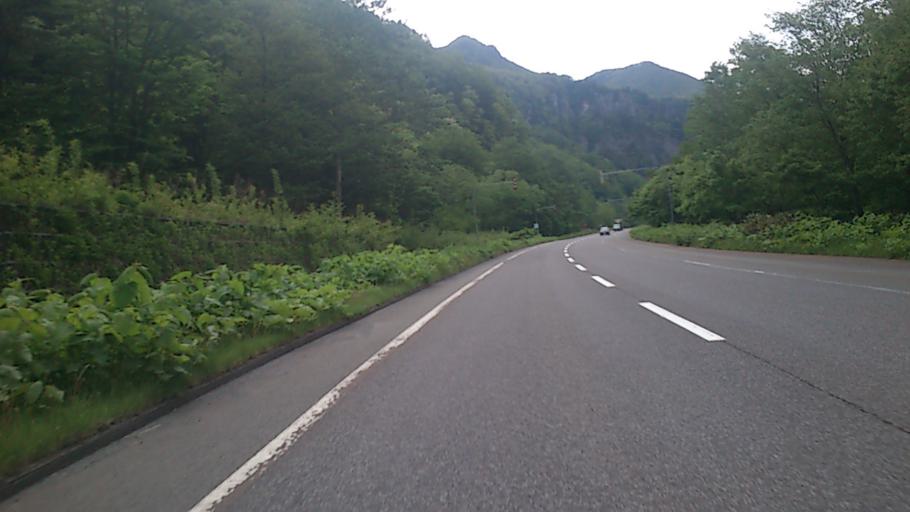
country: JP
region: Hokkaido
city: Kamikawa
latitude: 43.7567
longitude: 142.9251
